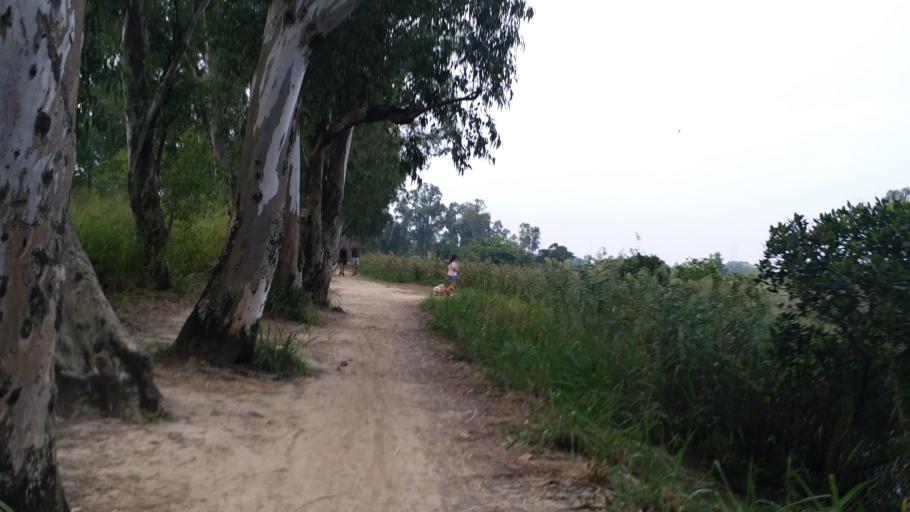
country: HK
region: Yuen Long
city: Yuen Long Kau Hui
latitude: 22.4570
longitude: 114.0344
